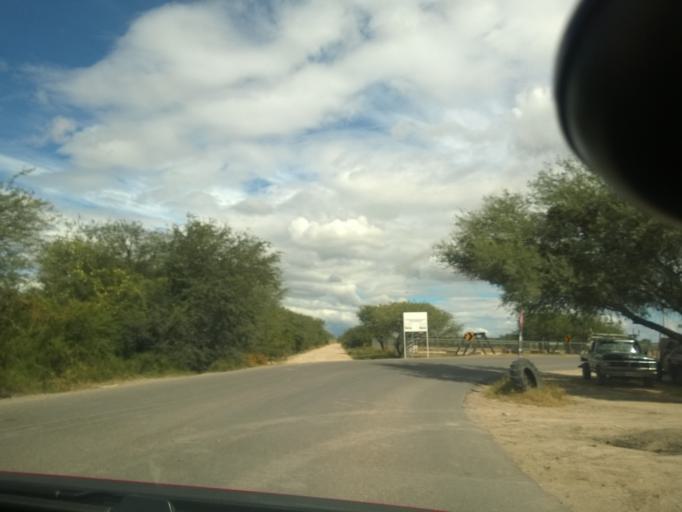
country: MX
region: Guanajuato
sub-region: Leon
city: Plan Guanajuato (La Sandia)
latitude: 20.9621
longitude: -101.6354
